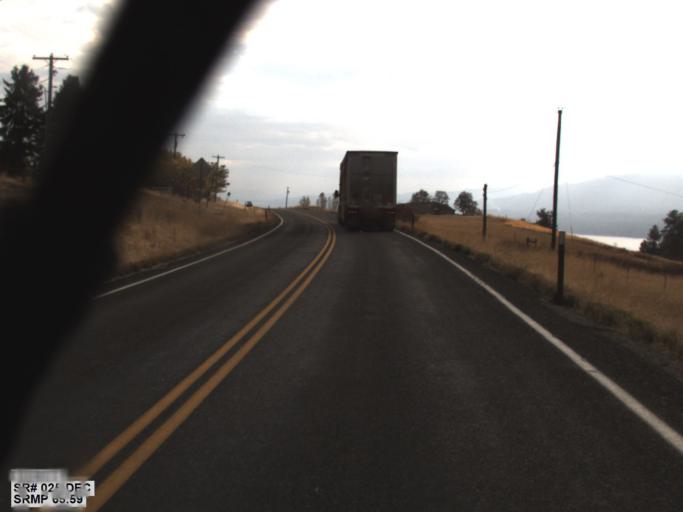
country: US
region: Washington
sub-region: Stevens County
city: Kettle Falls
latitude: 48.4183
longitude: -118.1718
